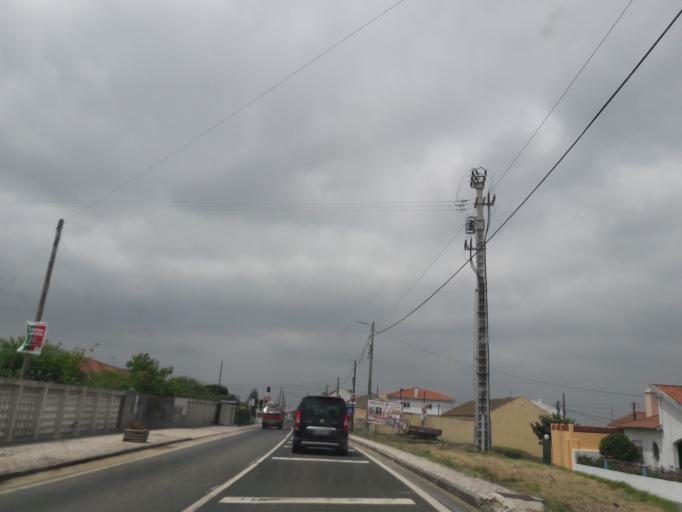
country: PT
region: Leiria
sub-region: Peniche
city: Atouguia da Baleia
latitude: 39.3329
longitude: -9.2666
